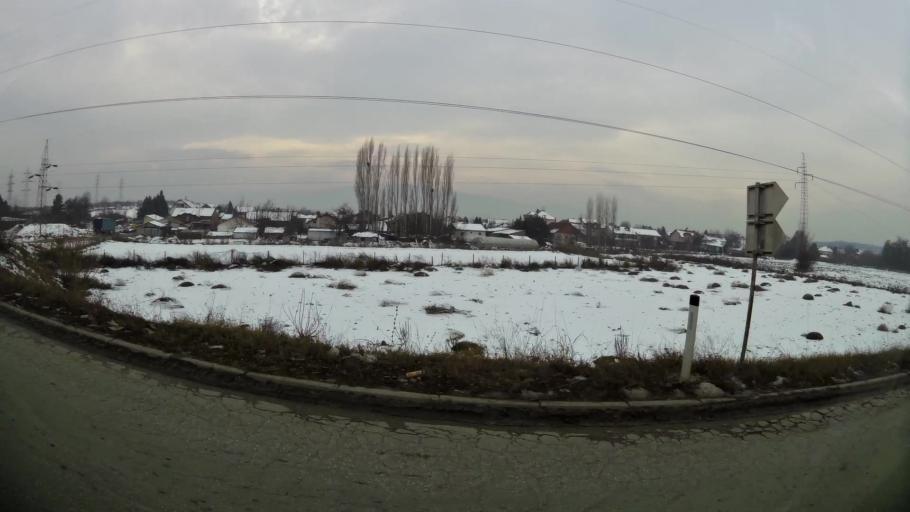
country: MK
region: Butel
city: Butel
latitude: 42.0399
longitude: 21.4543
